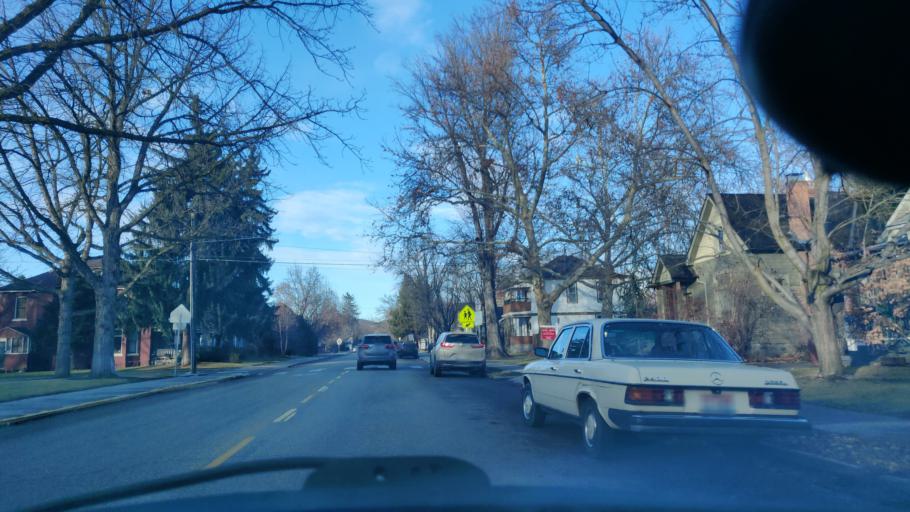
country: US
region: Idaho
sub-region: Ada County
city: Boise
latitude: 43.6262
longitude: -116.2034
